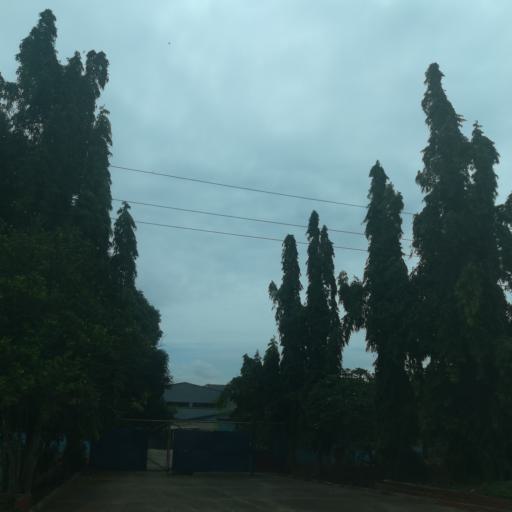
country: NG
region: Lagos
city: Ejirin
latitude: 6.6525
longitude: 3.7128
